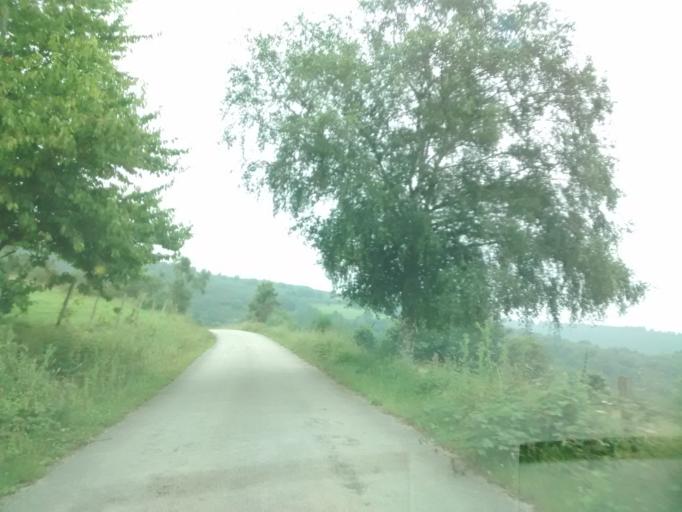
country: ES
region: Galicia
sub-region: Provincia de Ourense
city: Castro Caldelas
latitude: 42.4023
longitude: -7.3979
